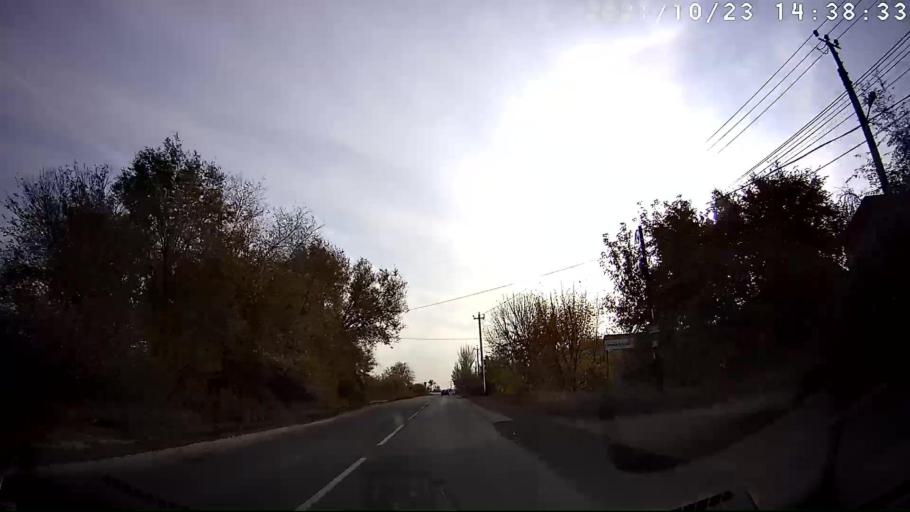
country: RU
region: Volgograd
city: Krasnoslobodsk
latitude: 48.4908
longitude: 44.5489
